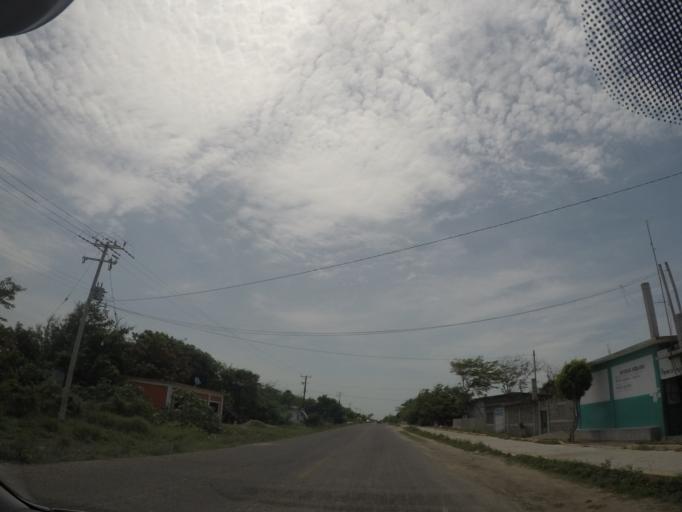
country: MX
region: Oaxaca
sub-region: San Mateo del Mar
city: Colonia Juarez
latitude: 16.2091
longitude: -95.0338
